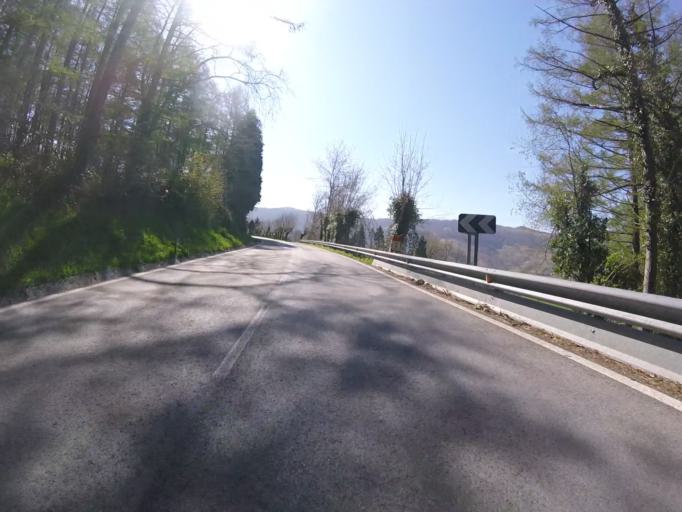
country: ES
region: Navarre
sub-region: Provincia de Navarra
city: Leitza
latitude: 43.0891
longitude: -1.8891
